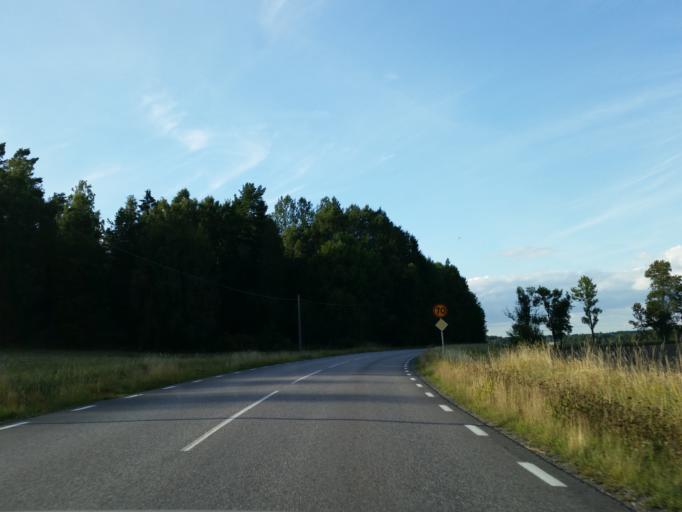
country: SE
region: Stockholm
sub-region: Sodertalje Kommun
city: Molnbo
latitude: 59.0080
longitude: 17.3763
